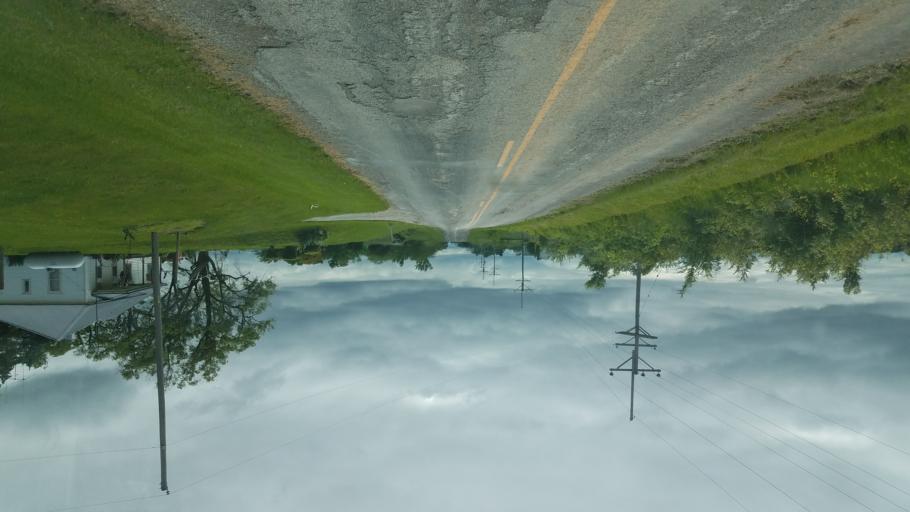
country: US
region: Iowa
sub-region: Decatur County
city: Lamoni
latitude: 40.4238
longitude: -93.8232
